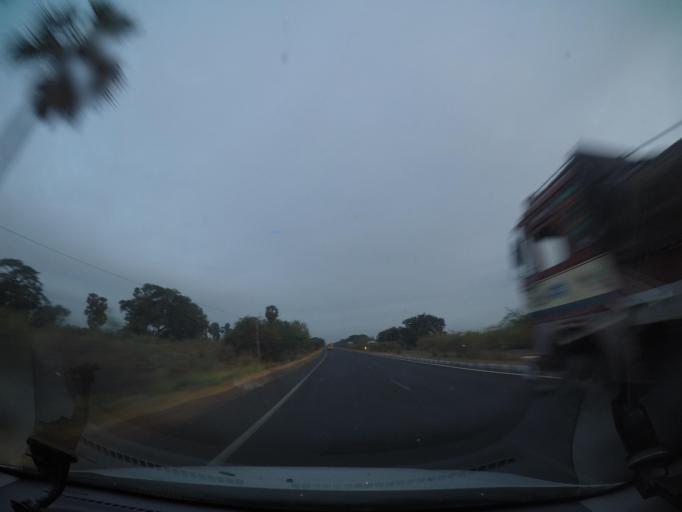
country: IN
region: Andhra Pradesh
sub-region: West Godavari
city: Tadepallegudem
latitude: 16.8101
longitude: 81.3466
